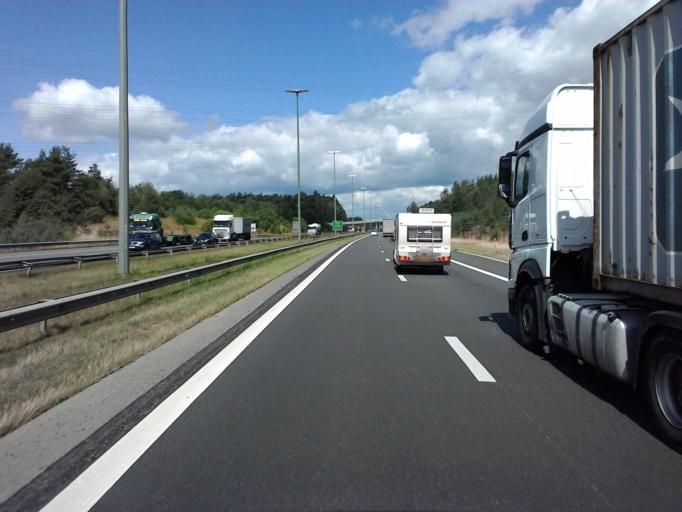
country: BE
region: Wallonia
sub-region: Province du Luxembourg
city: Arlon
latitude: 49.6762
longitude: 5.7652
